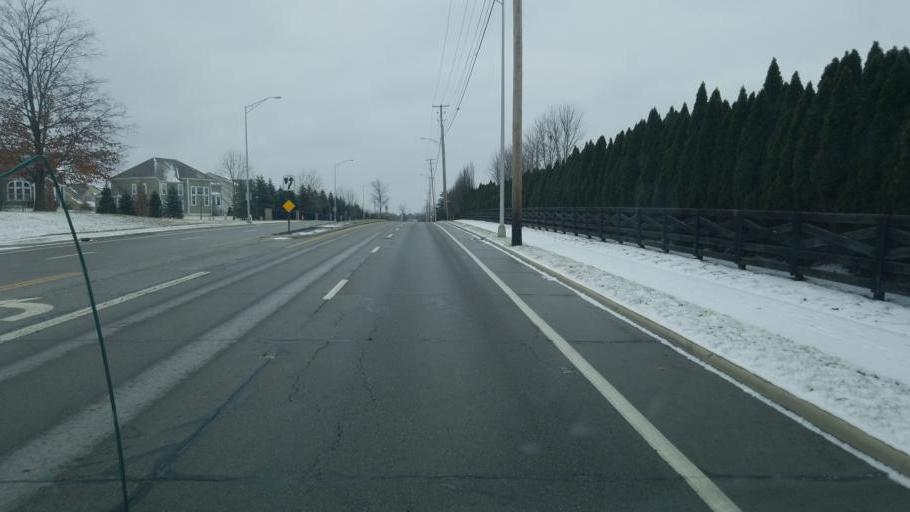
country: US
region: Ohio
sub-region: Franklin County
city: Worthington
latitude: 40.1168
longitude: -83.0498
